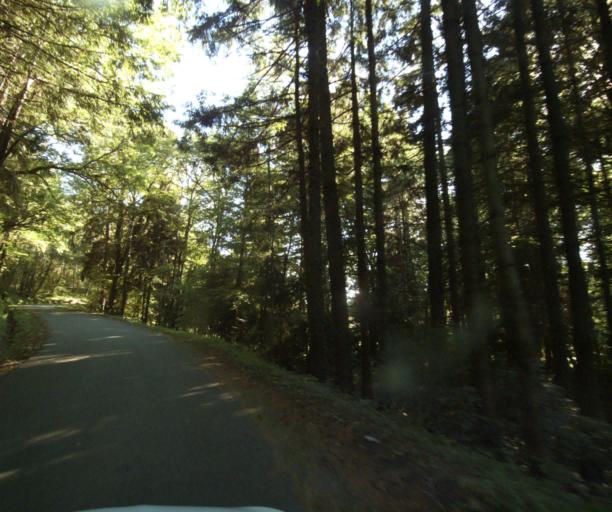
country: FR
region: Rhone-Alpes
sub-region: Departement de la Haute-Savoie
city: Massongy
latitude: 46.3079
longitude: 6.3407
